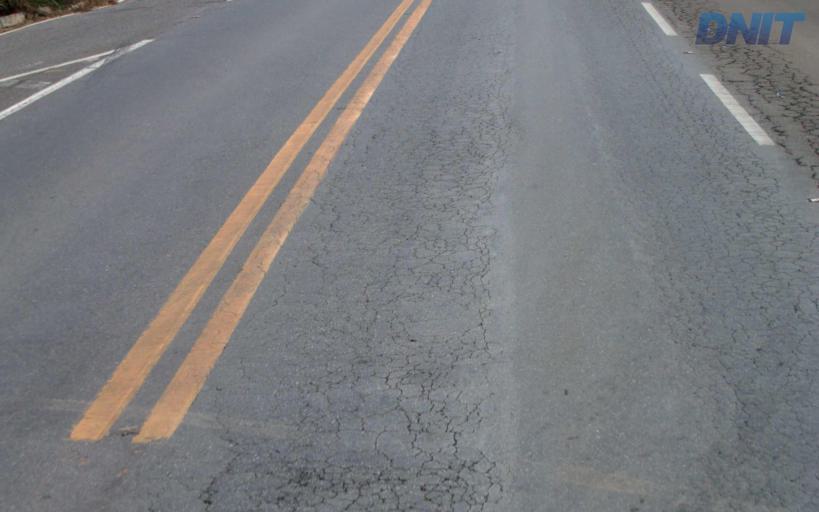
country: BR
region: Minas Gerais
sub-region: Governador Valadares
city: Governador Valadares
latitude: -19.0139
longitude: -42.1403
